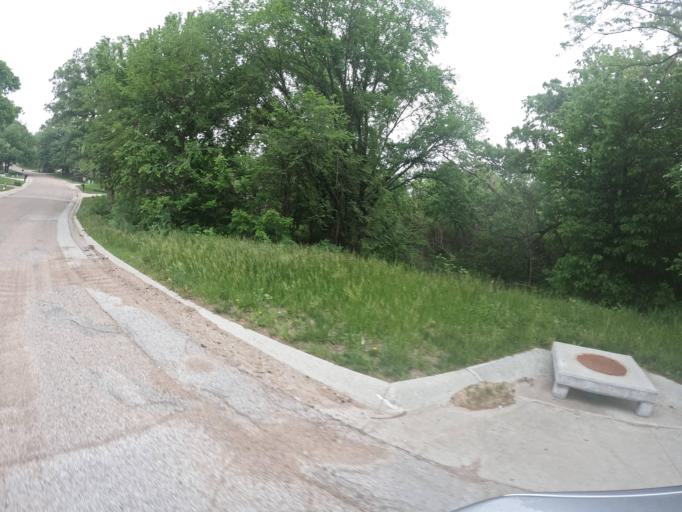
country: US
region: Nebraska
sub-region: Sarpy County
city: Offutt Air Force Base
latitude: 41.0472
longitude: -95.9654
